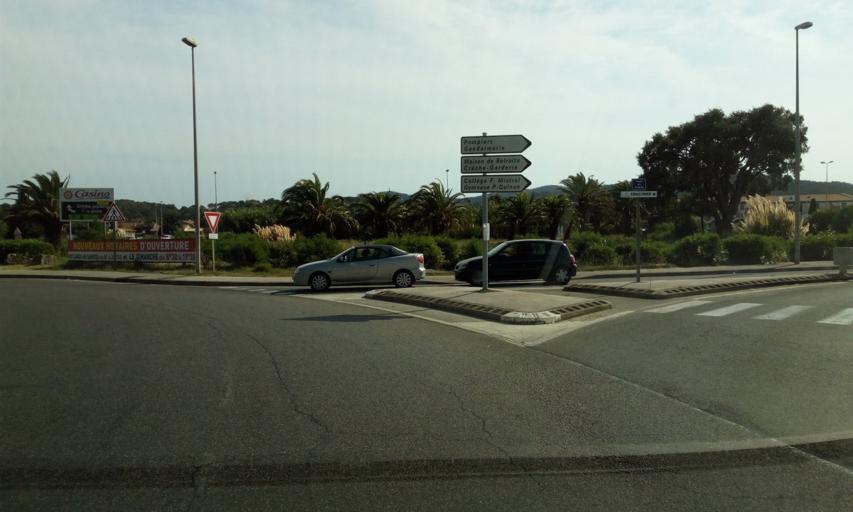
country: FR
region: Provence-Alpes-Cote d'Azur
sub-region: Departement du Var
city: Bormes-les-Mimosas
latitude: 43.1388
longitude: 6.3512
